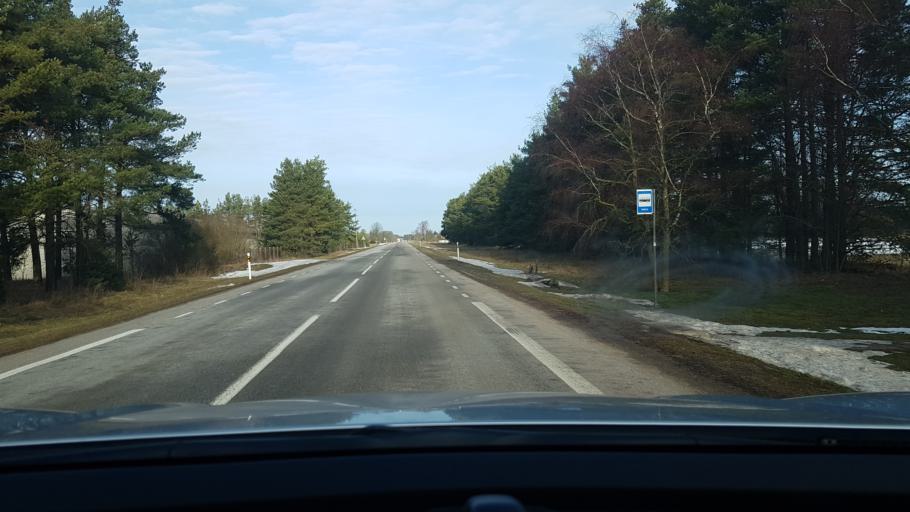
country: EE
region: Saare
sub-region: Kuressaare linn
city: Kuressaare
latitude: 58.5140
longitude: 22.7048
